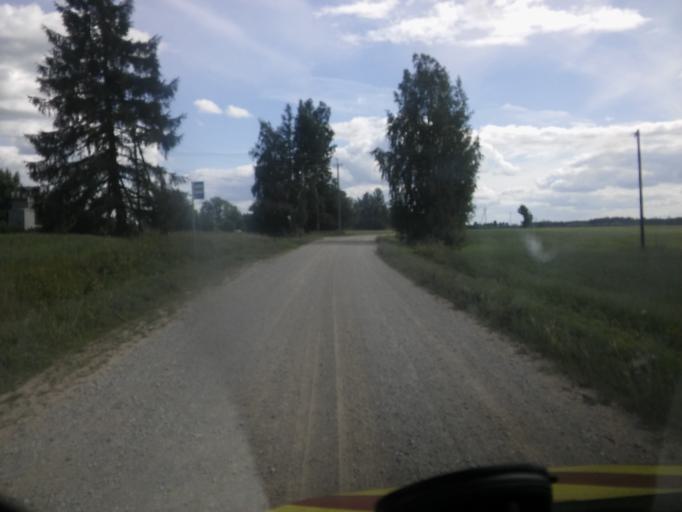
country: EE
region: Viljandimaa
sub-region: Karksi vald
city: Karksi-Nuia
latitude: 58.0750
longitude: 25.5200
